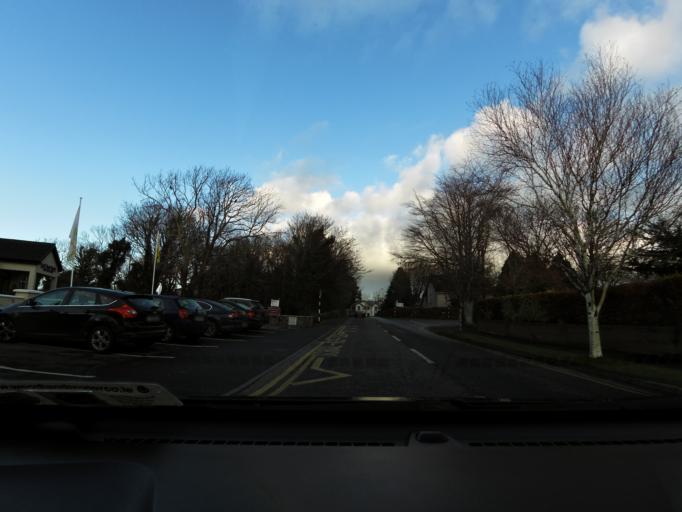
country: IE
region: Connaught
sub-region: County Galway
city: Oranmore
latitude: 53.2638
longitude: -8.9309
